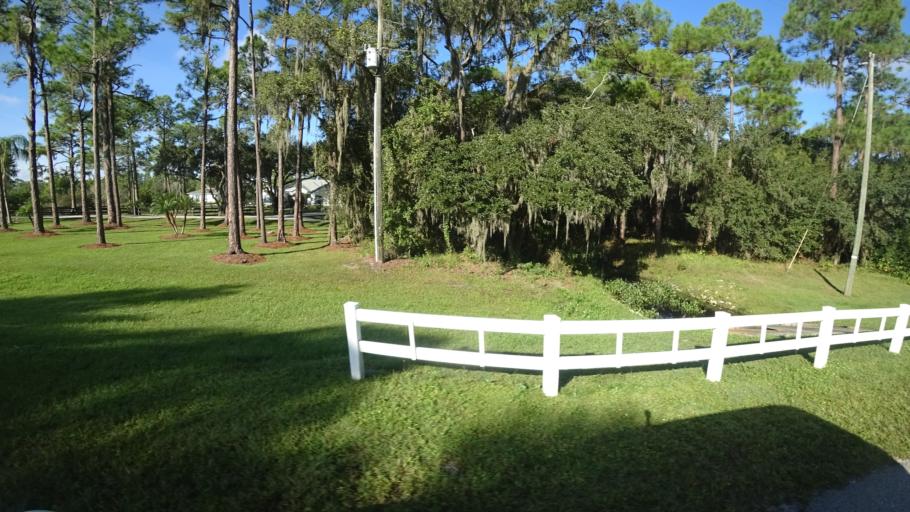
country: US
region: Florida
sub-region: Sarasota County
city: The Meadows
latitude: 27.4205
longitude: -82.3438
